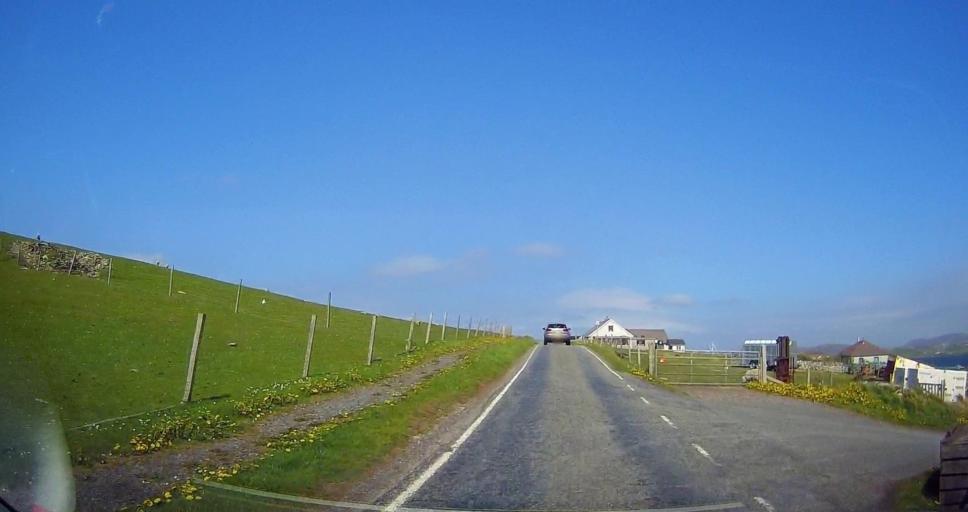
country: GB
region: Scotland
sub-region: Shetland Islands
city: Sandwick
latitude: 60.0982
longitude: -1.3211
